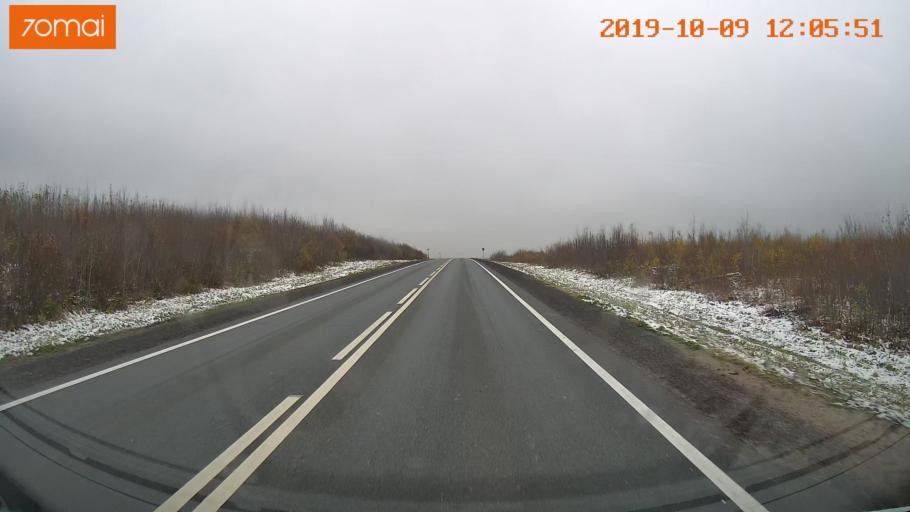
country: RU
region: Jaroslavl
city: Prechistoye
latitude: 58.6234
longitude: 40.3312
